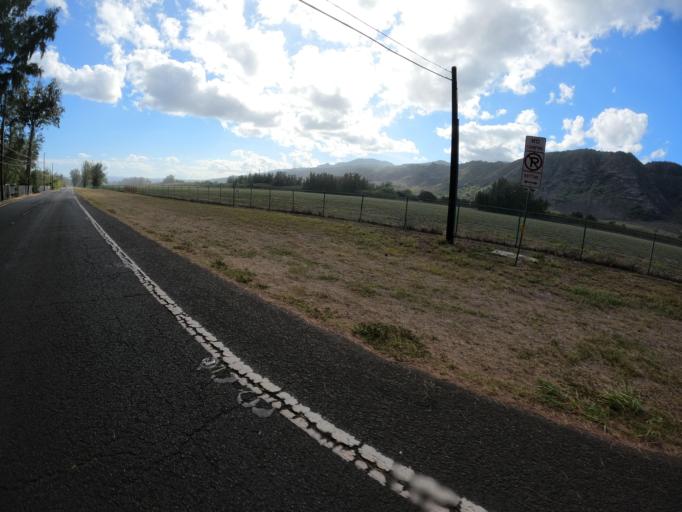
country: US
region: Hawaii
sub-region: Honolulu County
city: Mokuleia
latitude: 21.5811
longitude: -158.2018
